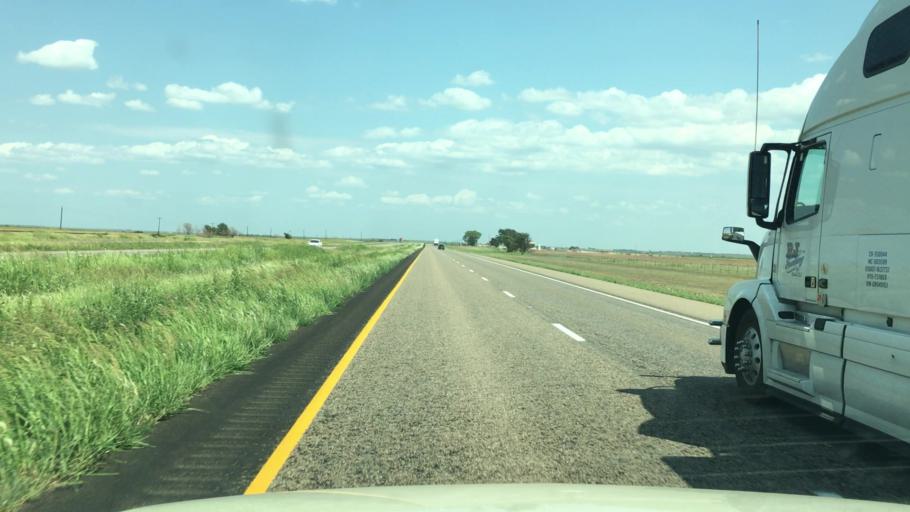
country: US
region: Texas
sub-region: Armstrong County
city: Claude
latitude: 35.0318
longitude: -101.1246
